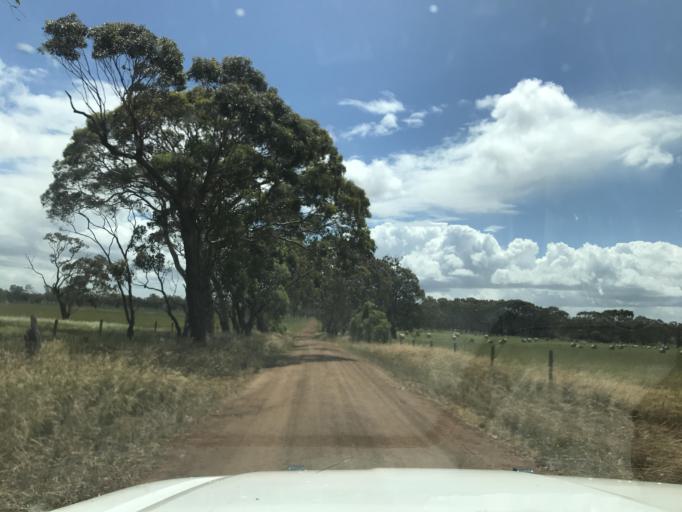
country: AU
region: South Australia
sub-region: Wattle Range
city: Penola
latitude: -37.1237
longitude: 141.2840
